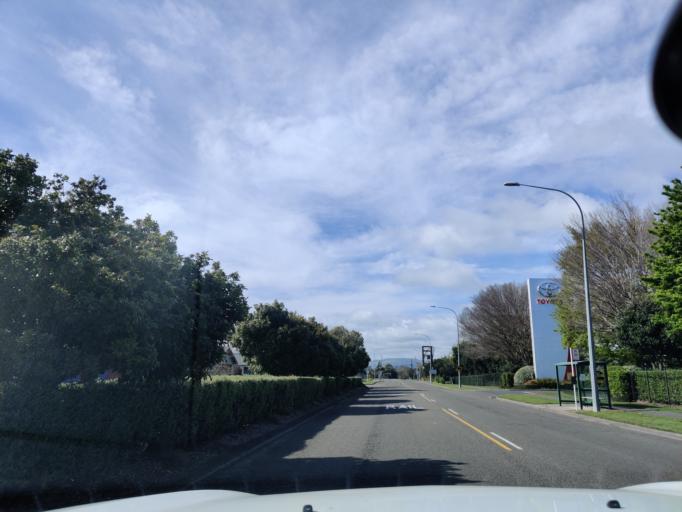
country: NZ
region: Manawatu-Wanganui
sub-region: Palmerston North City
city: Palmerston North
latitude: -40.3326
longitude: 175.6539
